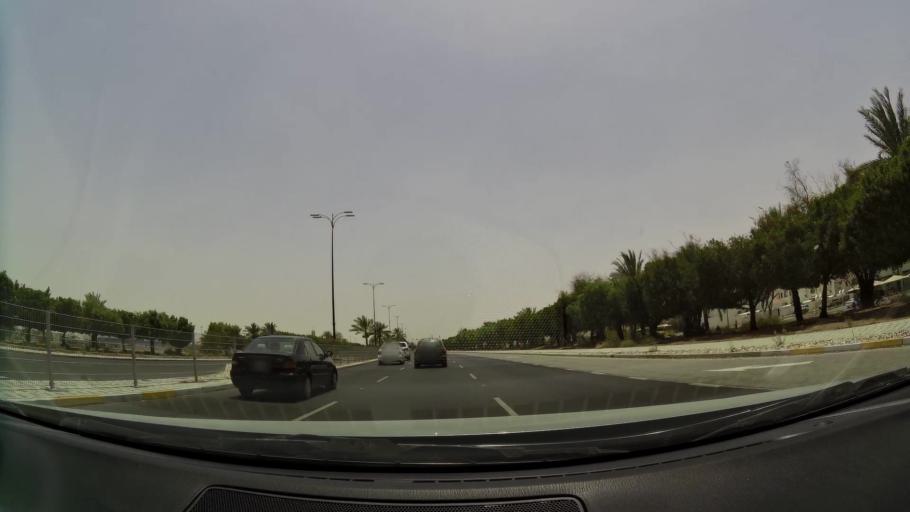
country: AE
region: Abu Dhabi
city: Al Ain
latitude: 24.2057
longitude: 55.7251
